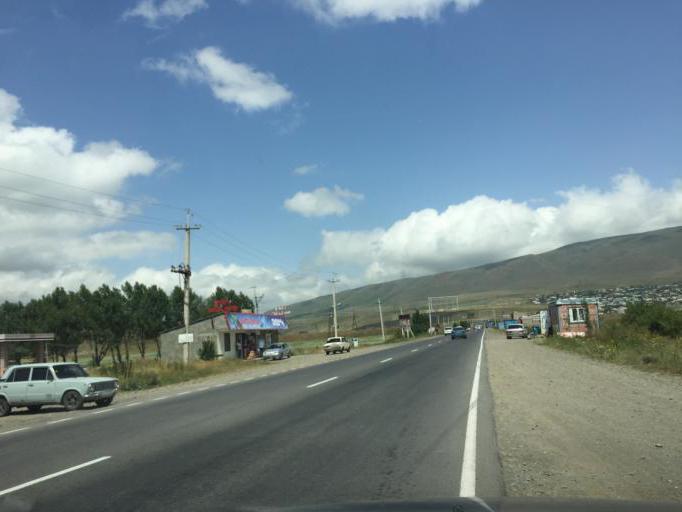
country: AM
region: Geghark'unik'i Marz
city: Tsovagyugh
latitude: 40.6101
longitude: 44.9545
